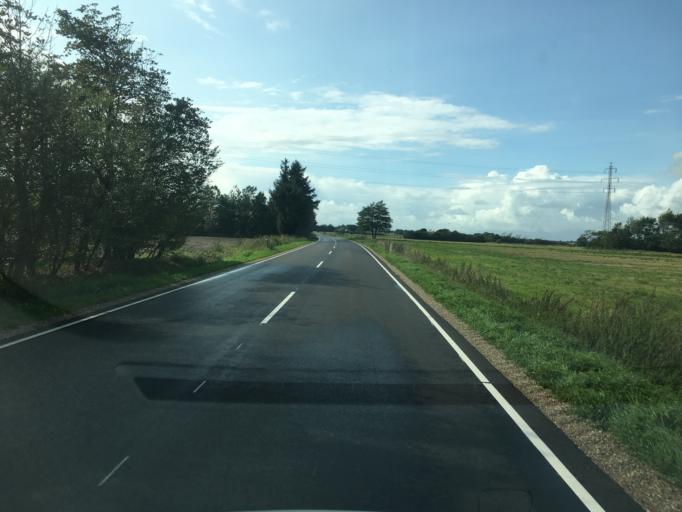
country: DK
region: South Denmark
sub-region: Tonder Kommune
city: Tonder
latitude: 55.0151
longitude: 8.8644
